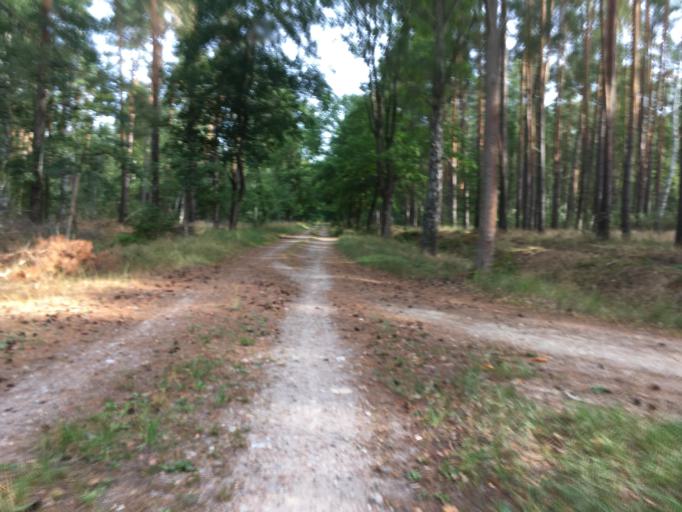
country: DE
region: Brandenburg
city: Marienwerder
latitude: 52.9647
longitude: 13.5304
